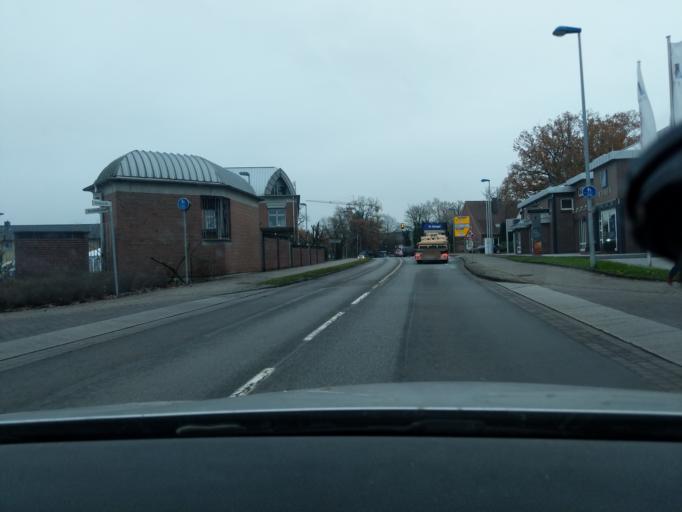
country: DE
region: Lower Saxony
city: Zeven
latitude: 53.2914
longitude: 9.2764
